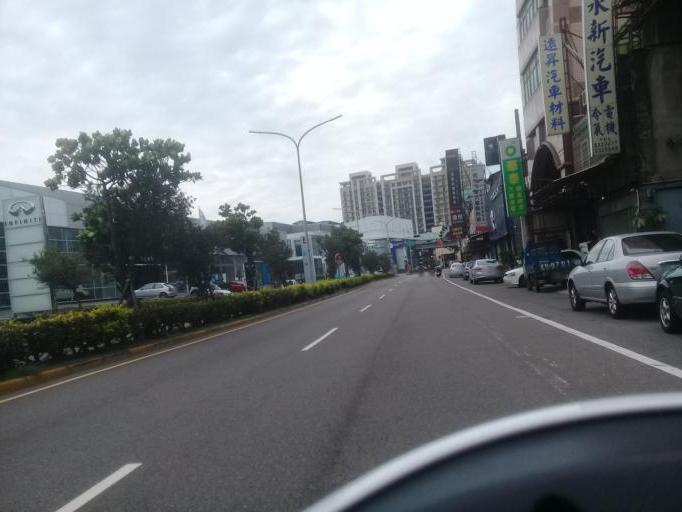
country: TW
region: Taiwan
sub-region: Hsinchu
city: Hsinchu
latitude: 24.8121
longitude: 120.9884
